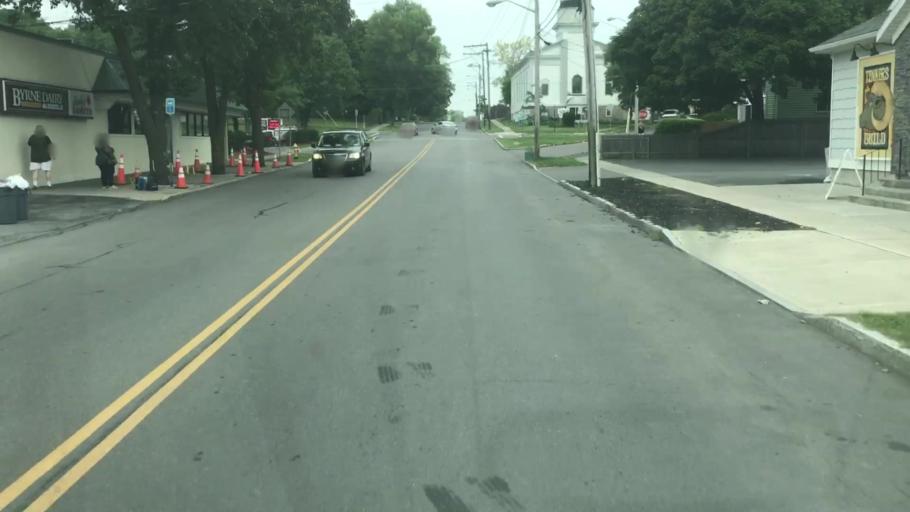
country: US
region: New York
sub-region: Cayuga County
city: Auburn
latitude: 42.9368
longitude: -76.5563
